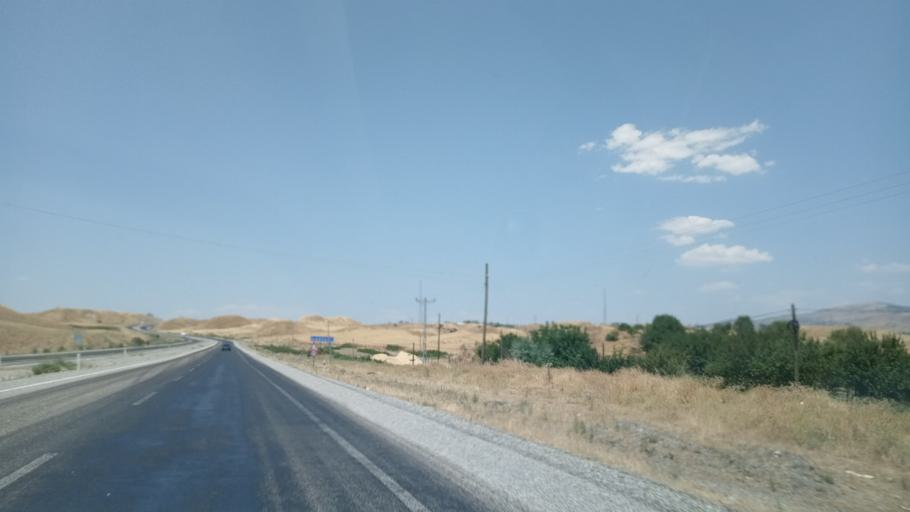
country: TR
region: Batman
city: Bekirhan
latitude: 38.1514
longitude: 41.3877
